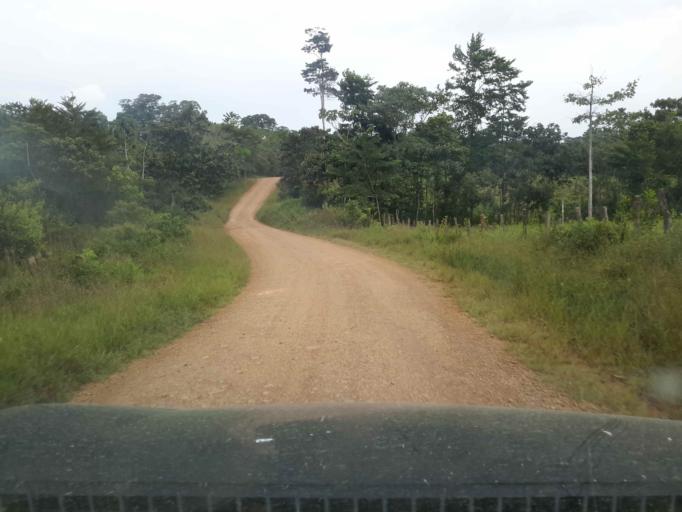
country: CR
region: Alajuela
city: Los Chiles
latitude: 11.0793
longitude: -84.5040
